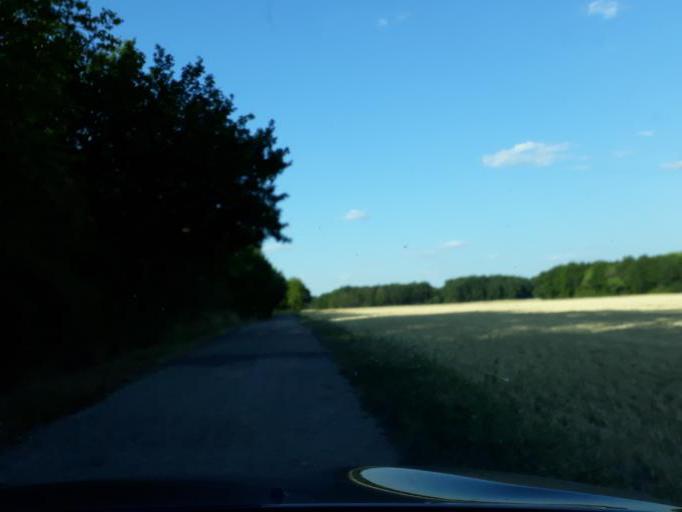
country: FR
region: Centre
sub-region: Departement du Loiret
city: Saint-Ay
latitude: 47.8808
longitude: 1.7332
